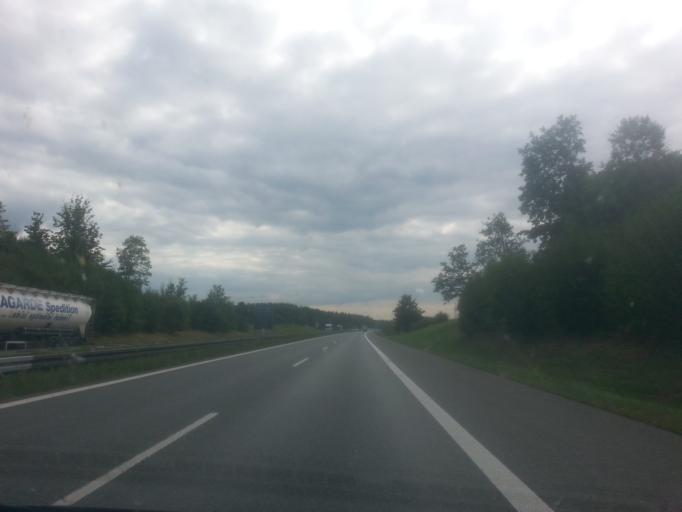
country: DE
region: Bavaria
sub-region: Upper Palatinate
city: Wackersdorf
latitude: 49.3077
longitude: 12.1524
